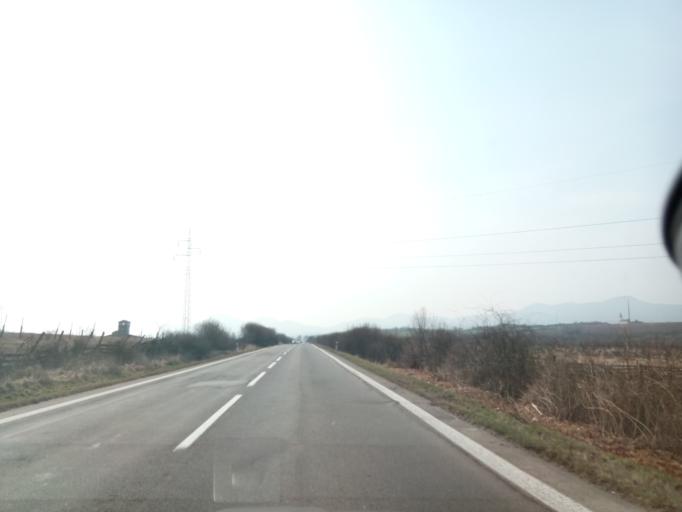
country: HU
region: Borsod-Abauj-Zemplen
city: Satoraljaujhely
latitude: 48.5013
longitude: 21.6527
